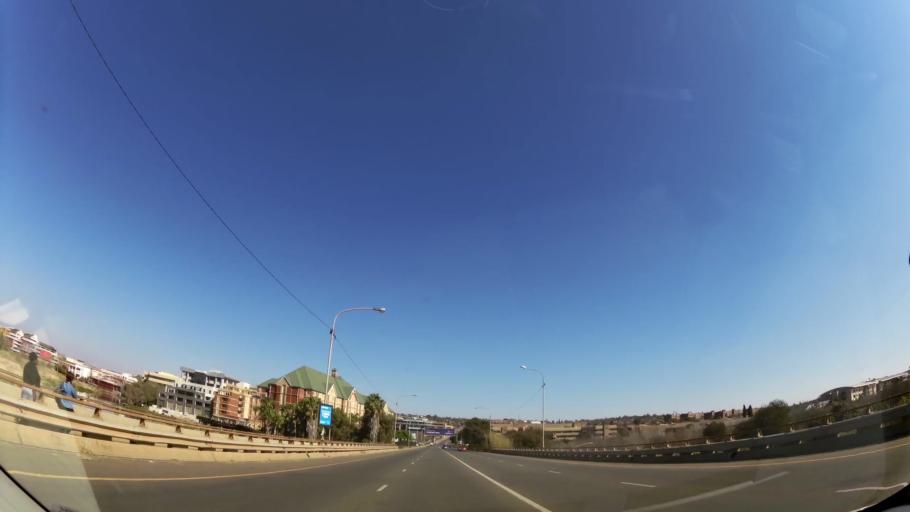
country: ZA
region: Gauteng
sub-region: City of Tshwane Metropolitan Municipality
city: Centurion
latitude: -25.8518
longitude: 28.1871
